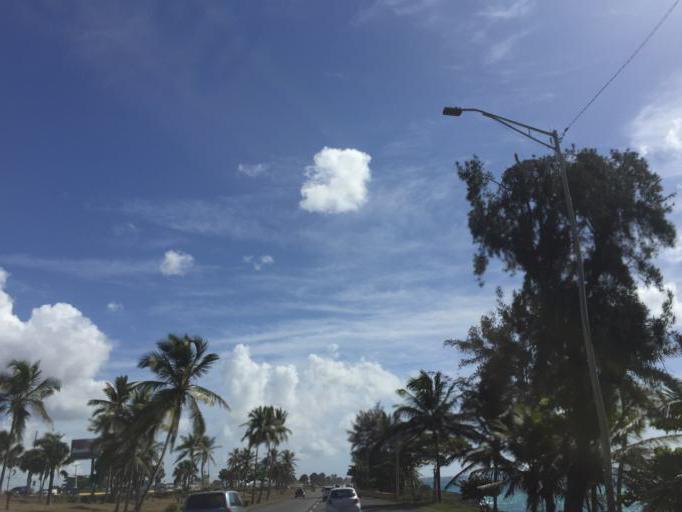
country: DO
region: Santo Domingo
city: Guerra
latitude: 18.4598
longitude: -69.7280
